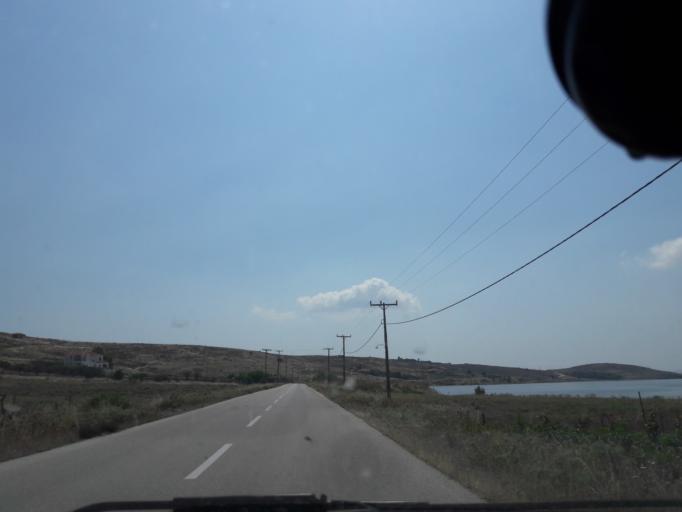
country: GR
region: North Aegean
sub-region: Nomos Lesvou
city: Myrina
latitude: 39.8619
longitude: 25.2620
